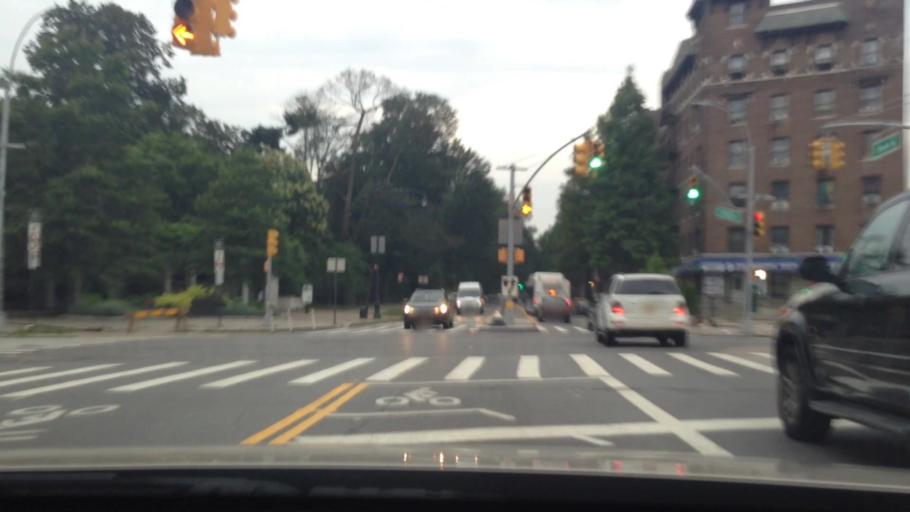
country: US
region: New York
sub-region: Kings County
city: Brooklyn
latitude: 40.6547
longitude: -73.9619
